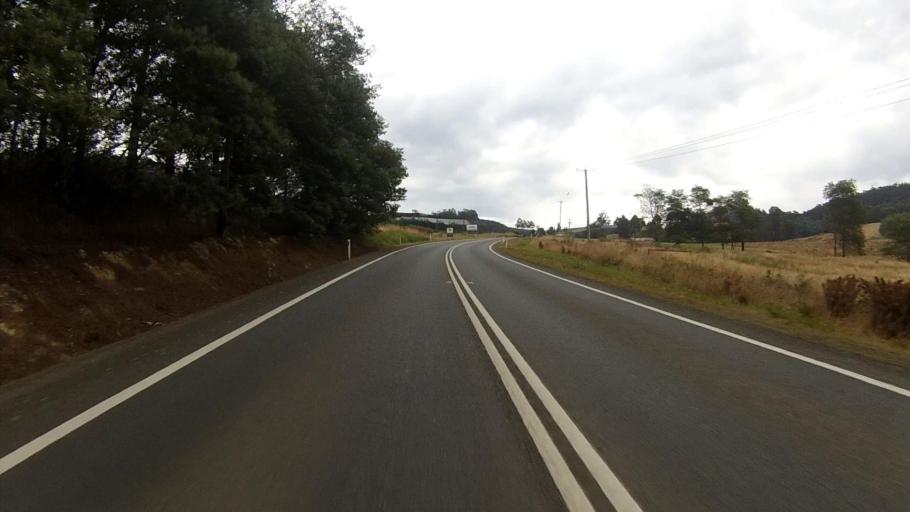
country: AU
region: Tasmania
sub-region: Huon Valley
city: Cygnet
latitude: -43.1343
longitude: 147.0524
